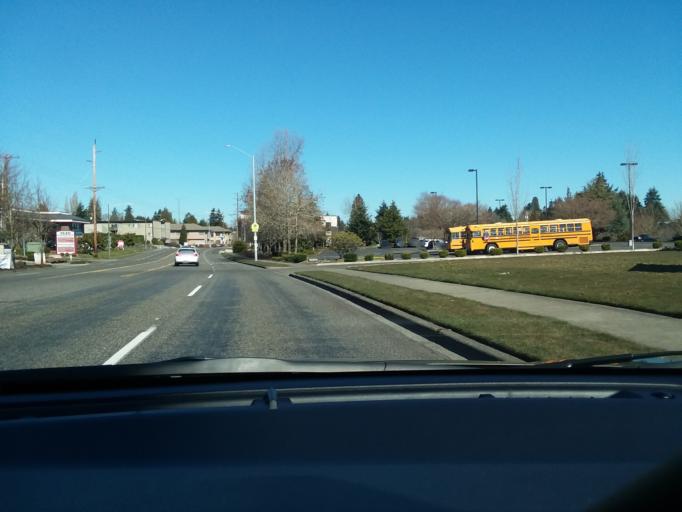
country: US
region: Washington
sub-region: Pierce County
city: Fircrest
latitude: 47.2449
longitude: -122.4830
